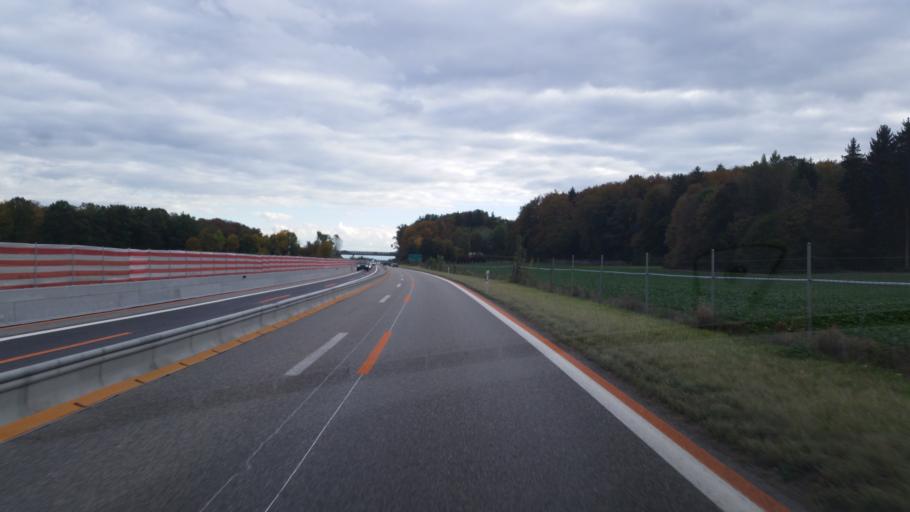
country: CH
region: Zurich
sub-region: Bezirk Buelach
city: Bachenbulach
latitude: 47.4983
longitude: 8.5356
